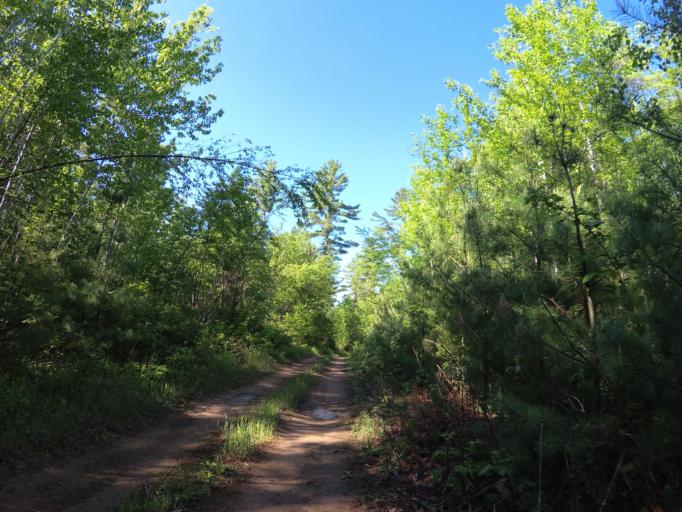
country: CA
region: Ontario
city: Renfrew
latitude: 45.1198
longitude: -77.0350
